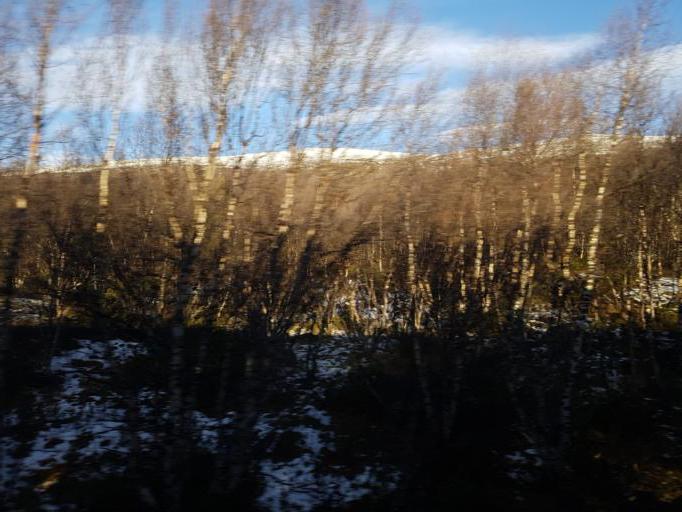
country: NO
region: Oppland
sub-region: Dovre
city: Dovre
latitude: 62.1935
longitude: 9.4942
